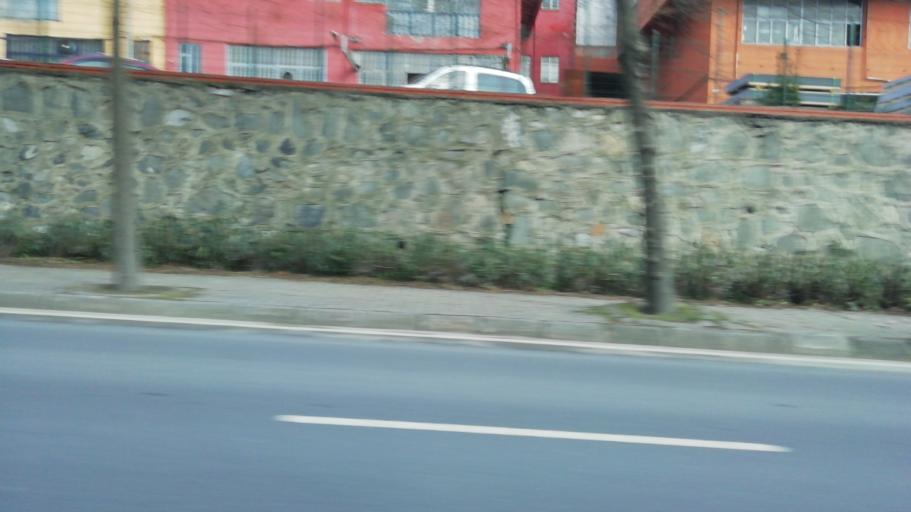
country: TR
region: Istanbul
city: Basaksehir
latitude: 41.0909
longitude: 28.7952
